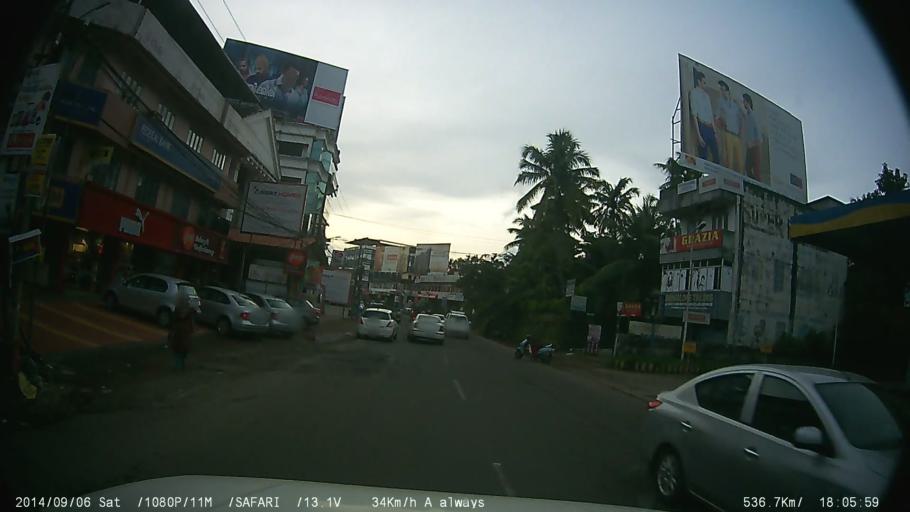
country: IN
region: Kerala
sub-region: Kottayam
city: Kottayam
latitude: 9.5882
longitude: 76.5395
